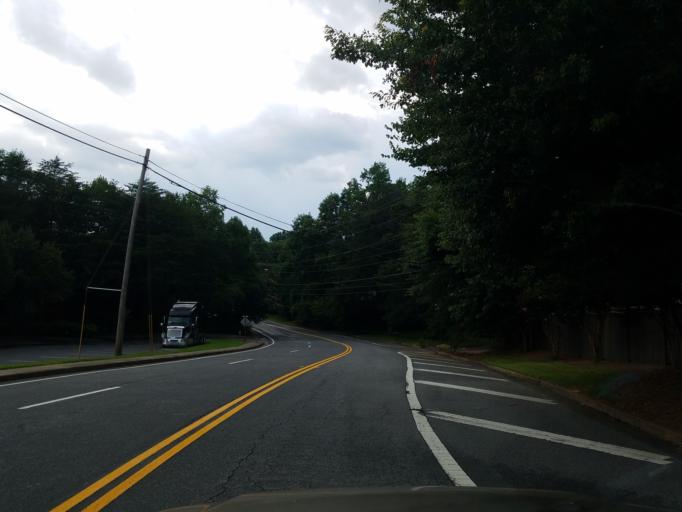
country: US
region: Georgia
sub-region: Cobb County
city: Marietta
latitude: 33.9724
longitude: -84.4886
